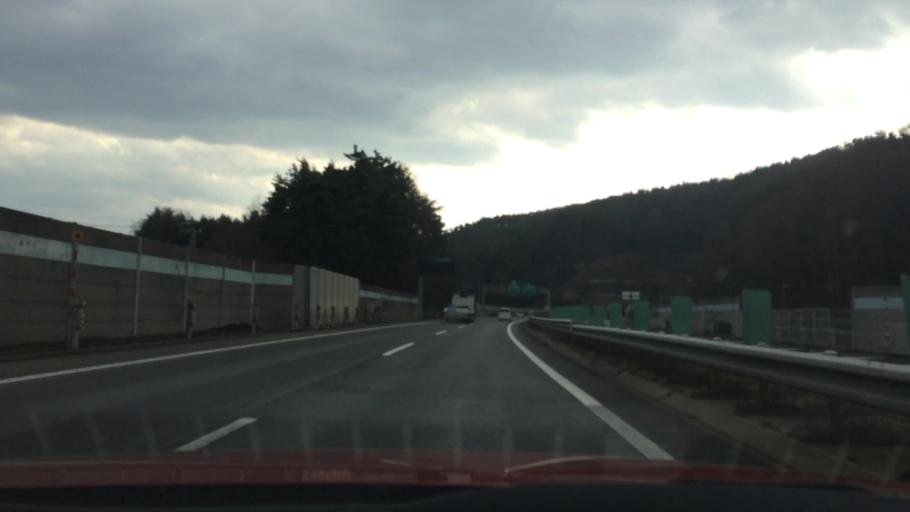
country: JP
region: Nagano
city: Okaya
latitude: 36.0756
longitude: 138.0388
